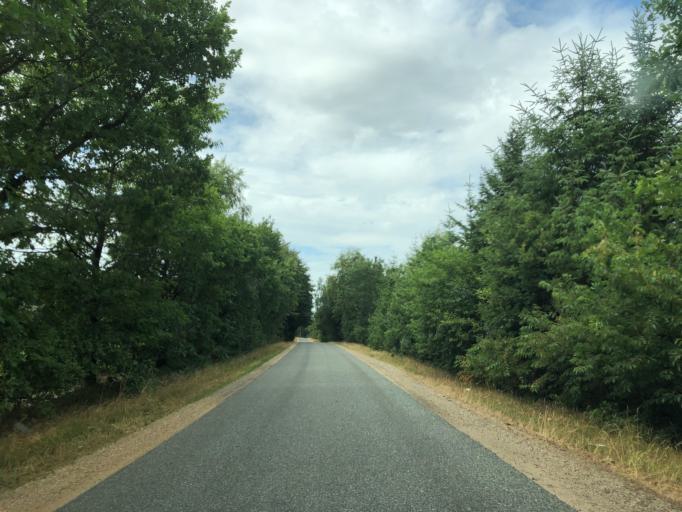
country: DK
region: South Denmark
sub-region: Billund Kommune
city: Grindsted
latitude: 55.6459
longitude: 8.9210
